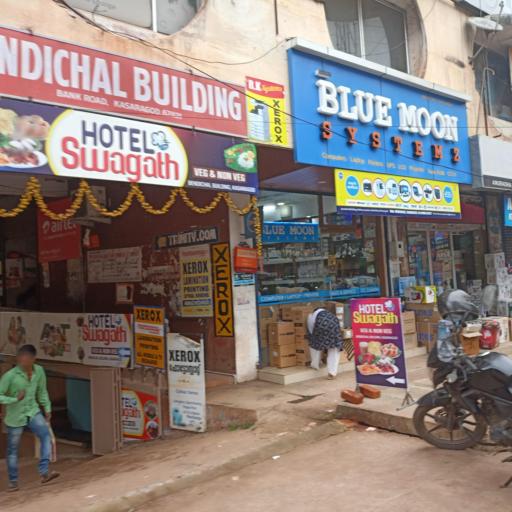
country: IN
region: Kerala
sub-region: Kasaragod District
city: Kasaragod
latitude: 12.5020
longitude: 74.9873
